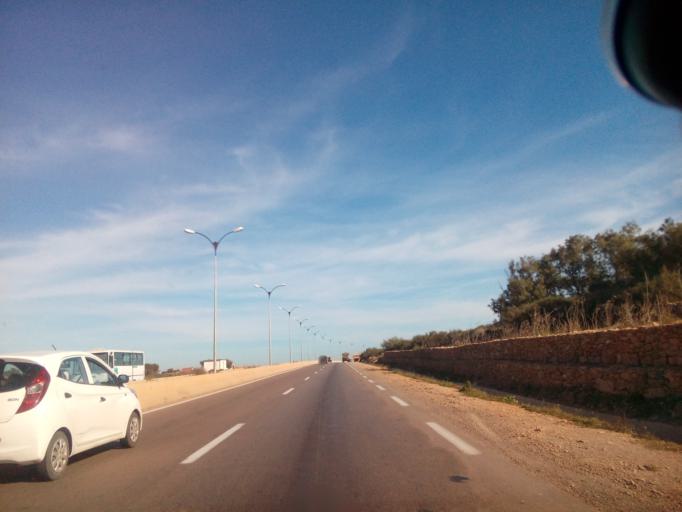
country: DZ
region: Oran
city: Ain el Bya
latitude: 35.7928
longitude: -0.0930
